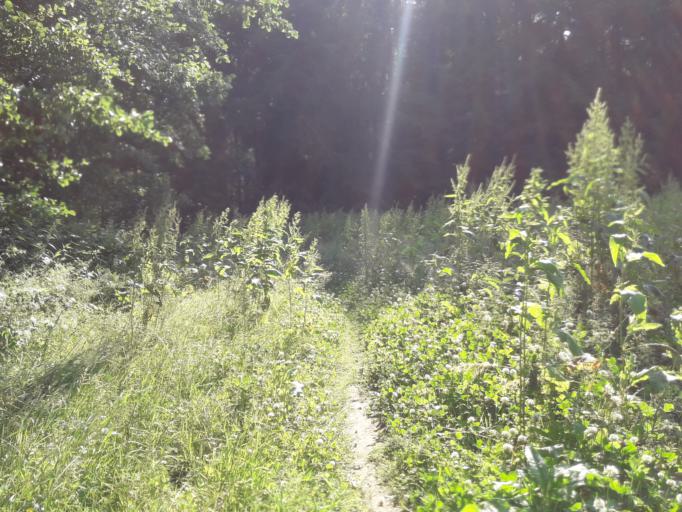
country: DE
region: North Rhine-Westphalia
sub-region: Regierungsbezirk Detmold
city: Salzkotten
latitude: 51.6812
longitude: 8.6572
